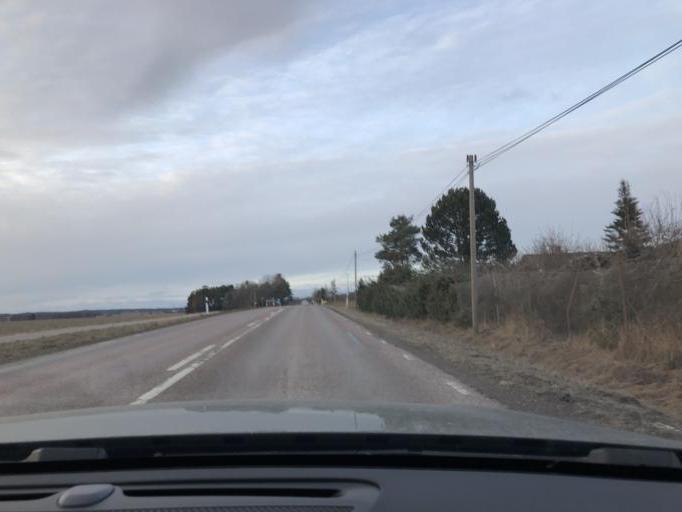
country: SE
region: Uppsala
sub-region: Uppsala Kommun
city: Gamla Uppsala
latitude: 59.9182
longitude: 17.6424
